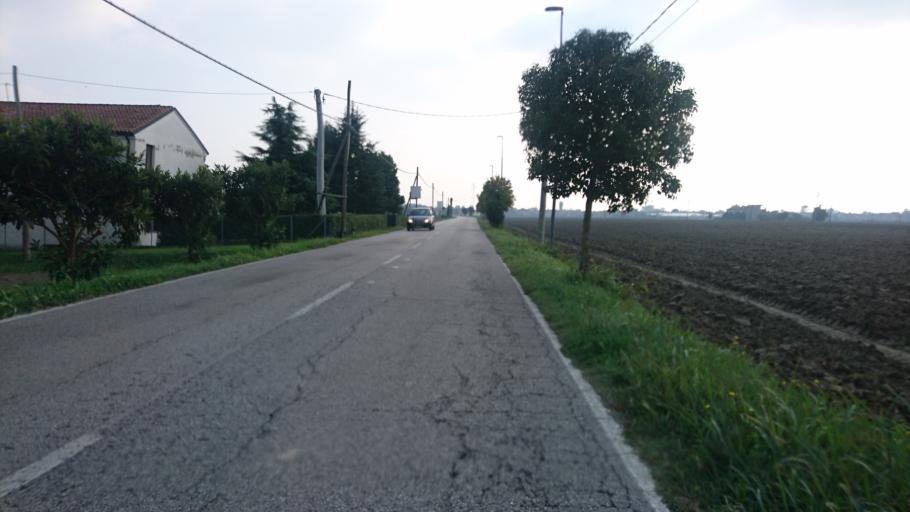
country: IT
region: Veneto
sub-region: Provincia di Rovigo
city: Arqua Polesine
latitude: 45.0195
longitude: 11.7415
